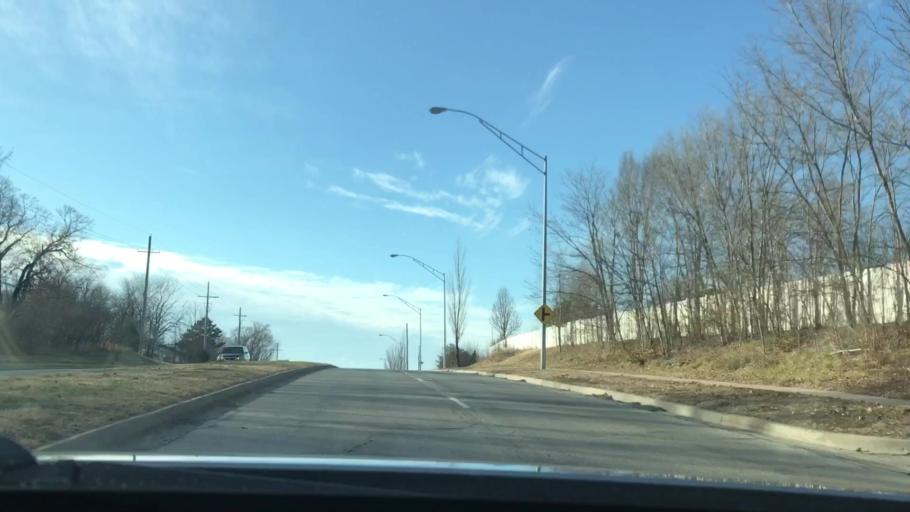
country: US
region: Missouri
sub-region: Platte County
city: Riverside
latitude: 39.2465
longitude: -94.6196
